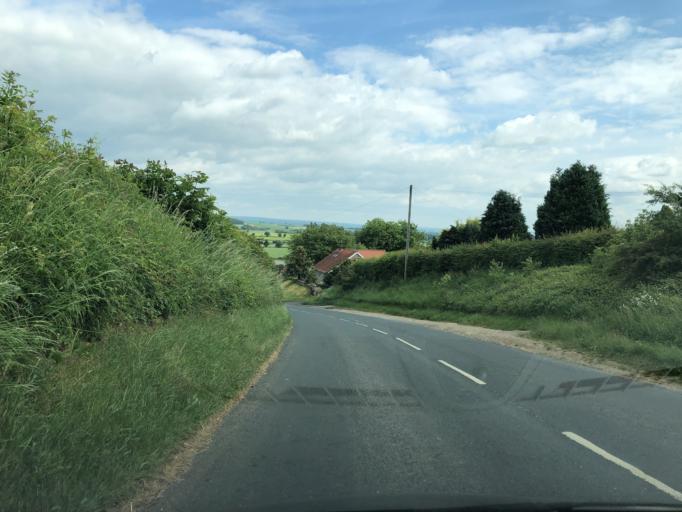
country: GB
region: England
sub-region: North Yorkshire
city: Helmsley
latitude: 54.1686
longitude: -0.9798
